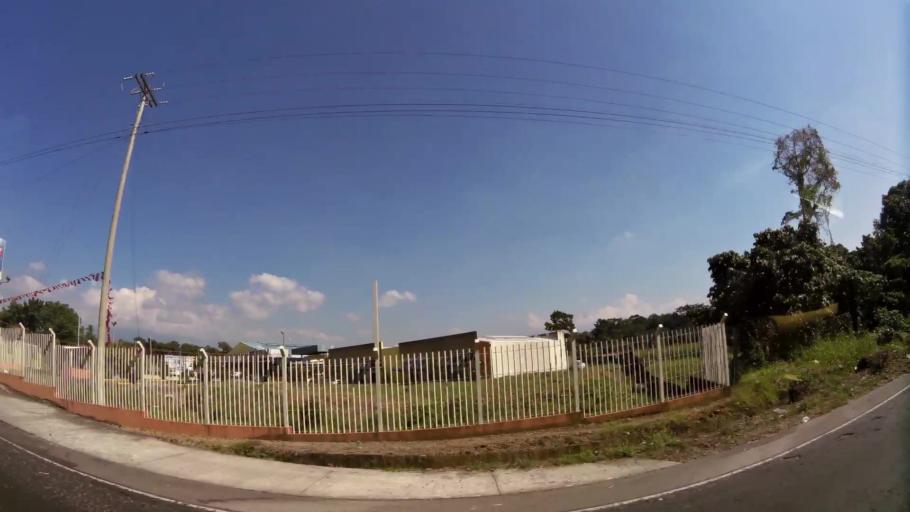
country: GT
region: Suchitepeque
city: Mazatenango
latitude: 14.5458
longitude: -91.5031
